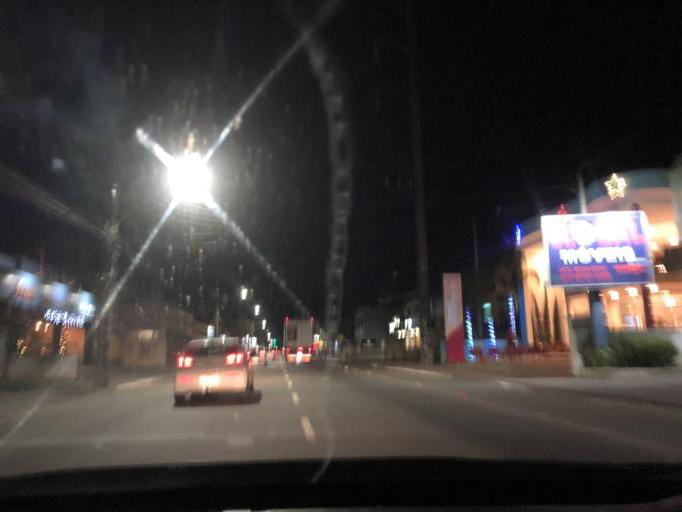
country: BR
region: Santa Catarina
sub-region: Jaragua Do Sul
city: Jaragua do Sul
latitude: -26.5121
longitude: -49.1182
